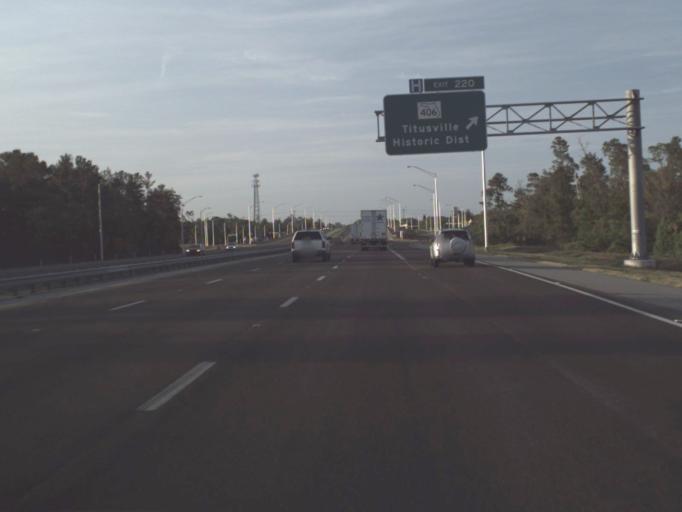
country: US
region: Florida
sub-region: Brevard County
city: Titusville
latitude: 28.6111
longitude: -80.8511
